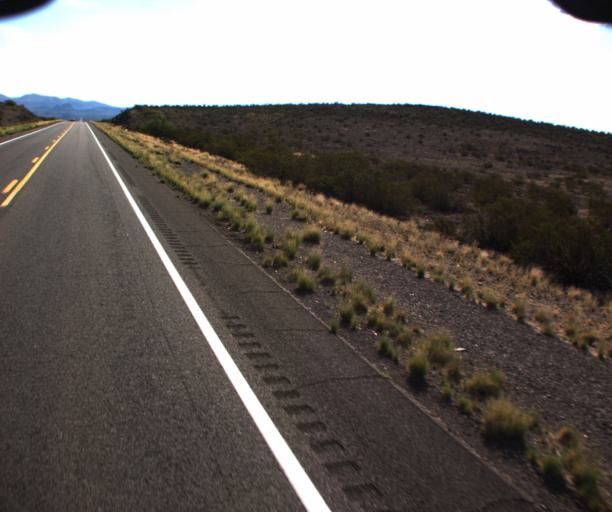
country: US
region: Arizona
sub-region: Graham County
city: Safford
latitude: 32.8085
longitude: -109.5075
